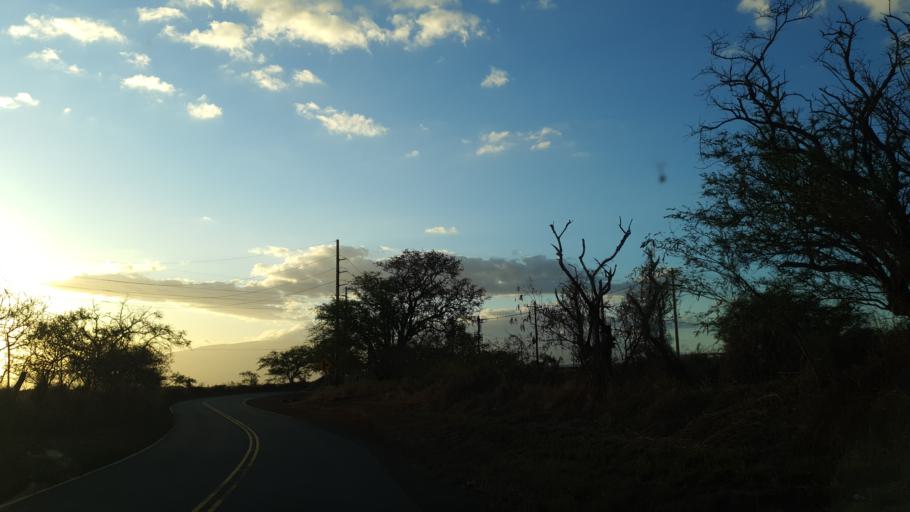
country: US
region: Hawaii
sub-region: Maui County
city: Pukalani
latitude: 20.7864
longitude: -156.3494
